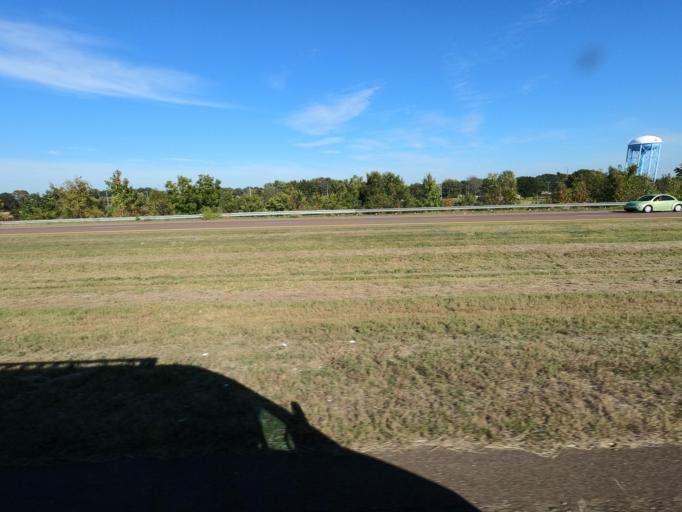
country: US
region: Tennessee
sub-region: Dyer County
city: Dyersburg
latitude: 36.0683
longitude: -89.3448
